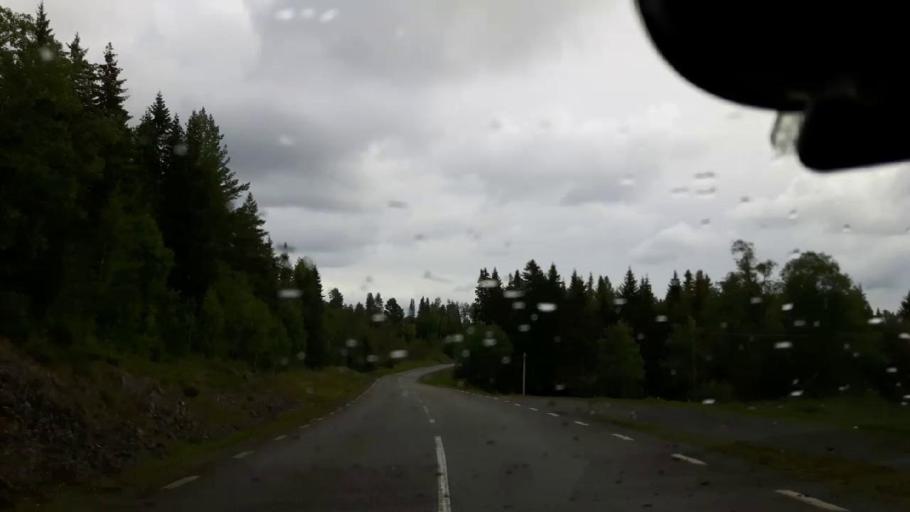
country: SE
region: Jaemtland
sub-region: Krokoms Kommun
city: Valla
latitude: 63.4154
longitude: 13.8008
